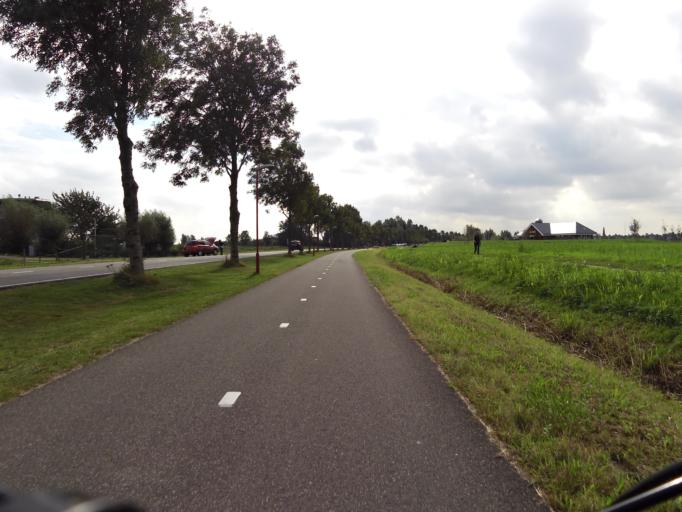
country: NL
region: South Holland
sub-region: Gemeente Rijnwoude
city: Benthuizen
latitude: 52.0856
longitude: 4.5157
